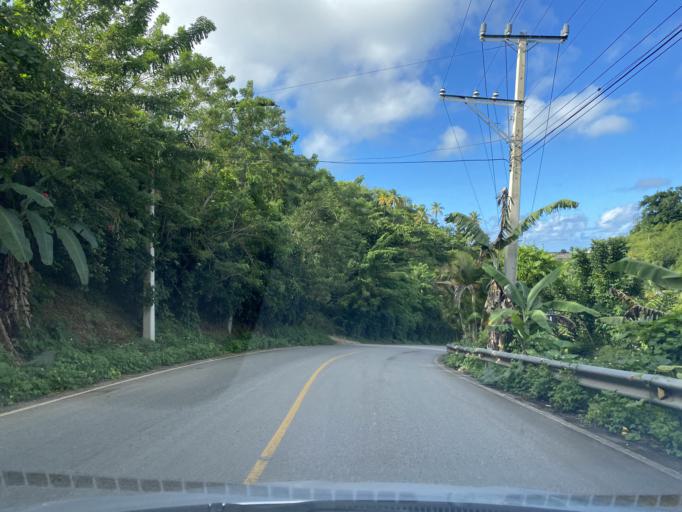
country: DO
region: Samana
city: Las Terrenas
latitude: 19.2813
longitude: -69.5542
